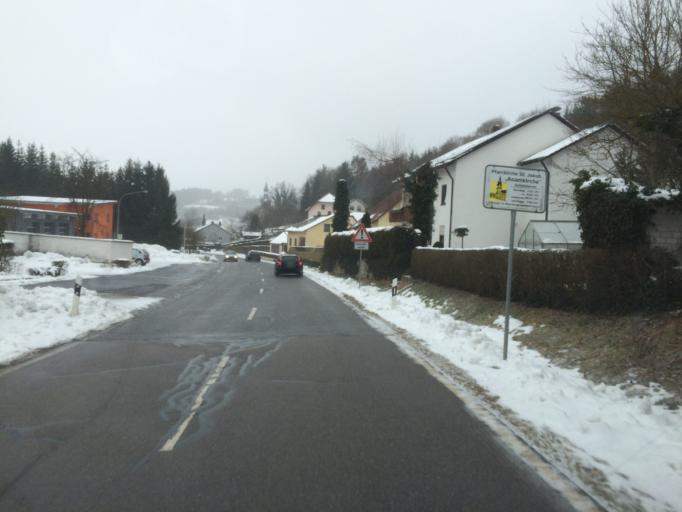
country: DE
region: Bavaria
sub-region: Upper Palatinate
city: Ensdorf
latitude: 49.3444
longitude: 11.9401
